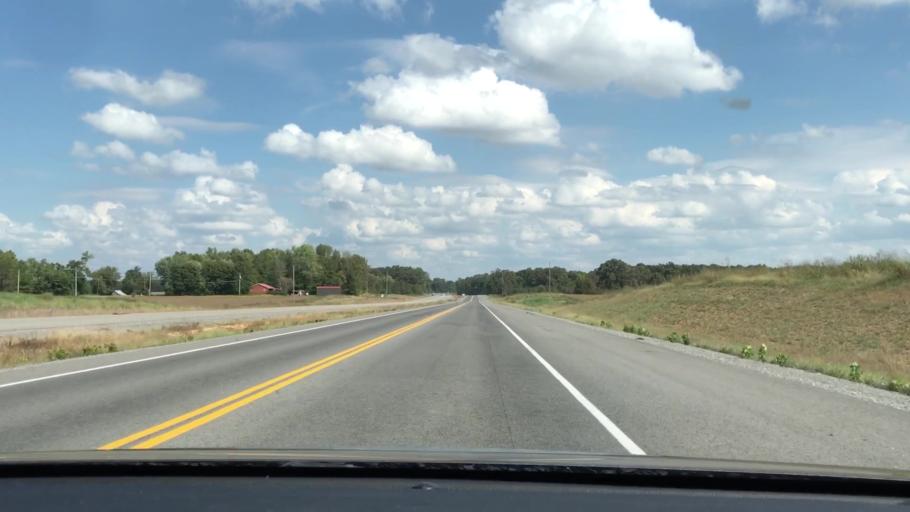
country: US
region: Kentucky
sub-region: Trigg County
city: Cadiz
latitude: 36.8269
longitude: -87.8694
